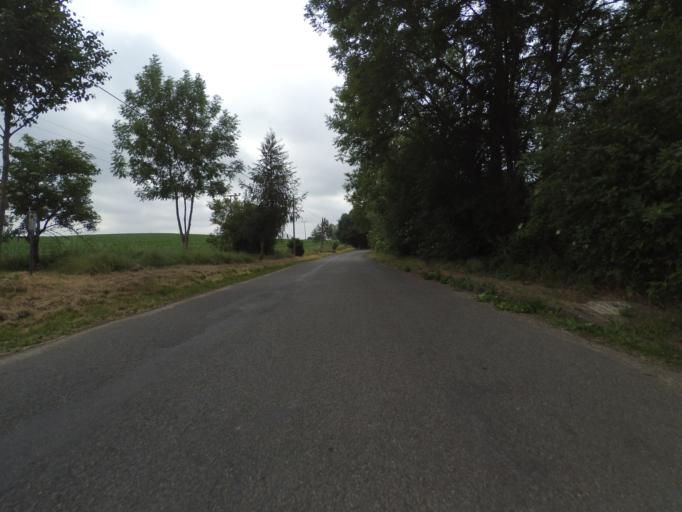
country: DE
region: Mecklenburg-Vorpommern
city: Krakow am See
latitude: 53.6628
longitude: 12.3493
